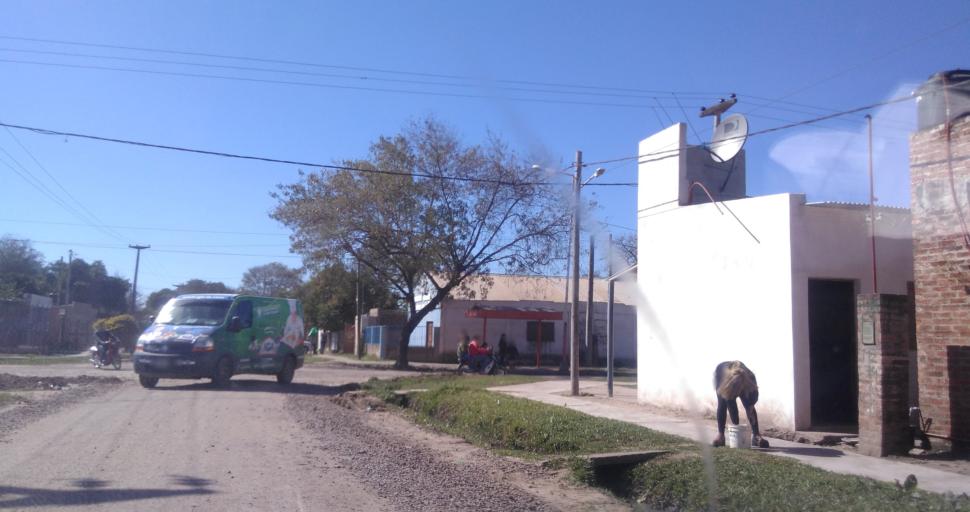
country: AR
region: Chaco
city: Fontana
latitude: -27.4499
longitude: -59.0384
